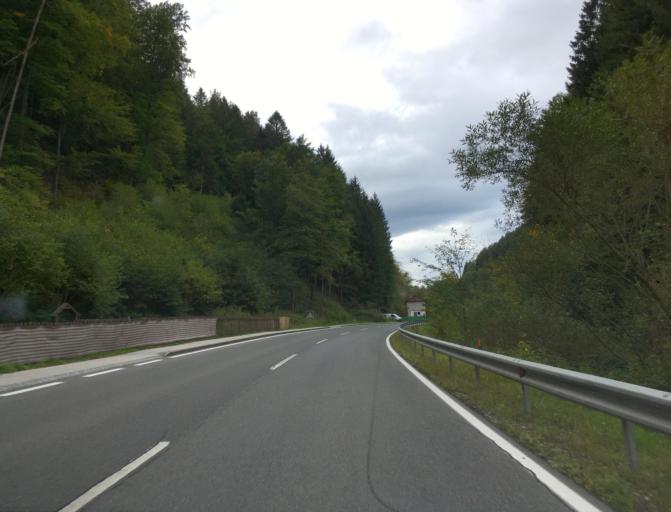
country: AT
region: Lower Austria
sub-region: Politischer Bezirk Neunkirchen
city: Edlitz
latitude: 47.5785
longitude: 16.1425
